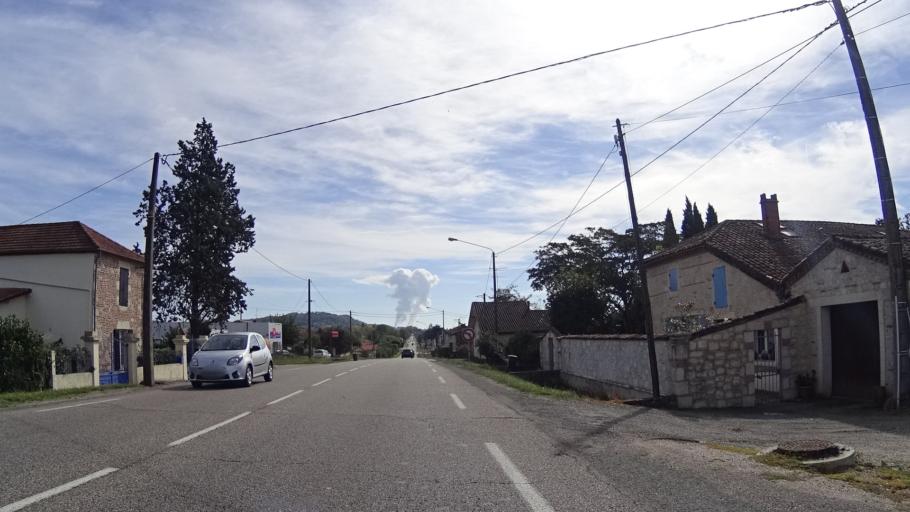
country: FR
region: Aquitaine
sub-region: Departement du Lot-et-Garonne
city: Castelculier
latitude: 44.1737
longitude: 0.6893
